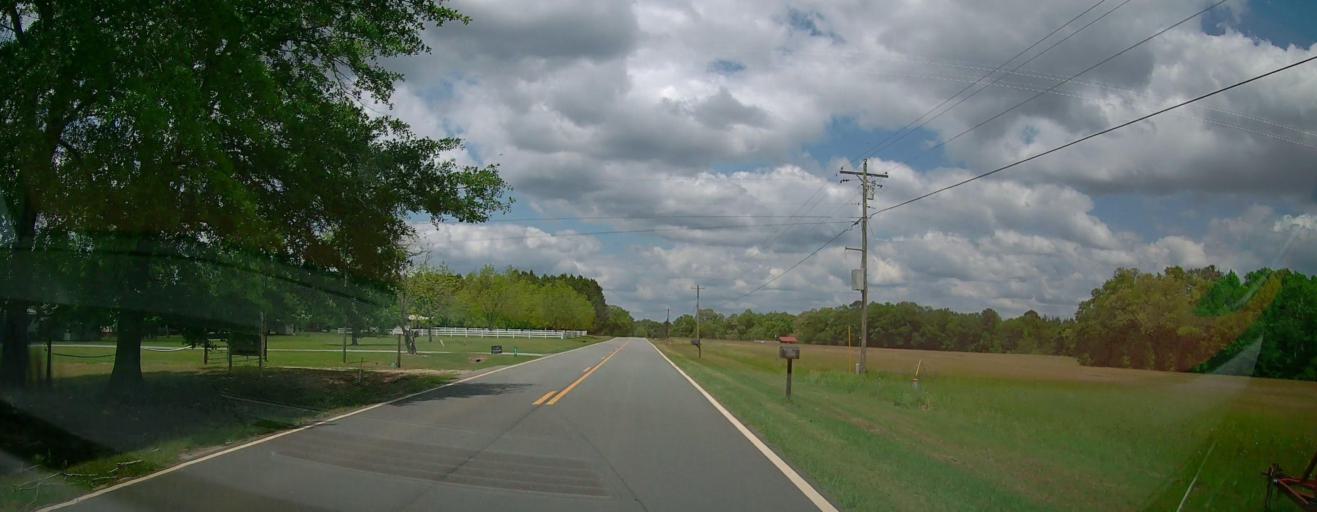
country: US
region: Georgia
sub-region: Laurens County
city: Dublin
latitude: 32.6130
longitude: -82.9677
